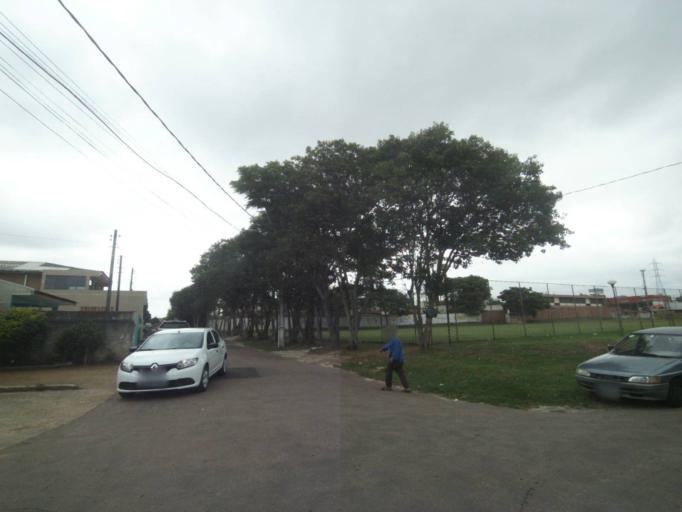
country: BR
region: Parana
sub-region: Sao Jose Dos Pinhais
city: Sao Jose dos Pinhais
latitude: -25.5426
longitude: -49.2713
